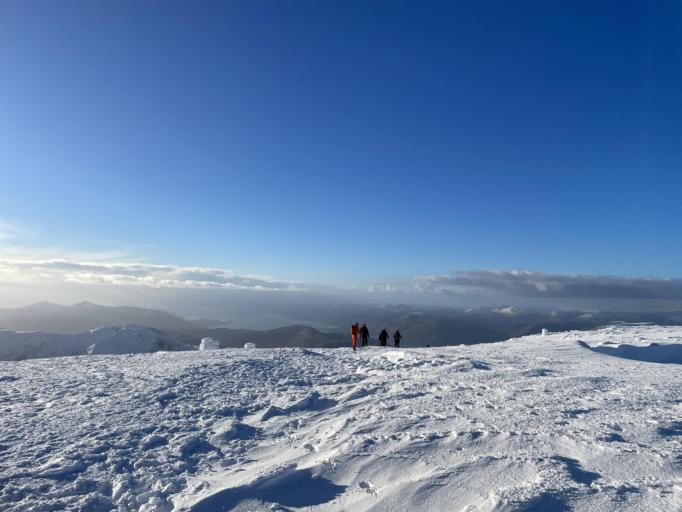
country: GB
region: Scotland
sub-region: Highland
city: Fort William
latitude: 56.7962
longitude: -5.0047
